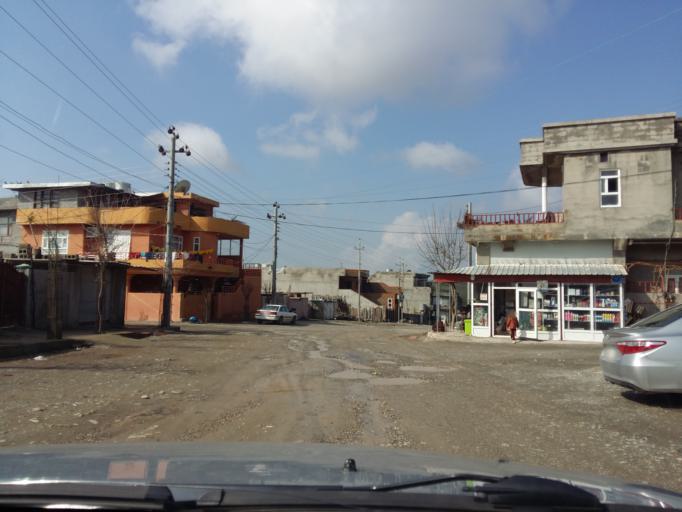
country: IQ
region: As Sulaymaniyah
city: Qeladize
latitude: 36.1935
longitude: 45.1249
